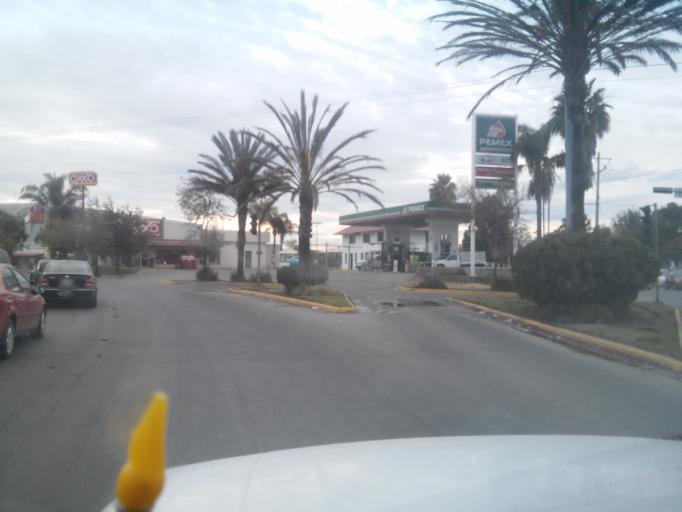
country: MX
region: Durango
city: Victoria de Durango
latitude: 24.0025
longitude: -104.6531
